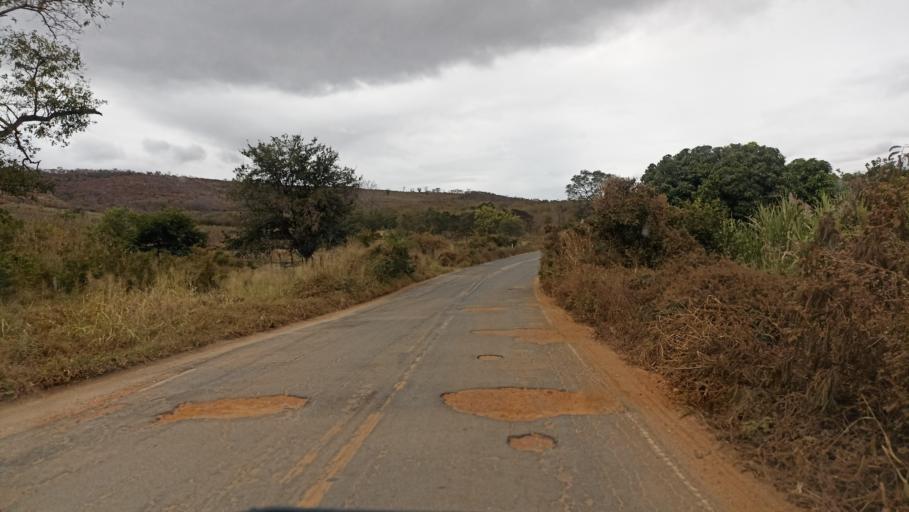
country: BR
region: Minas Gerais
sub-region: Itinga
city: Itinga
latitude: -16.6462
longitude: -41.8289
